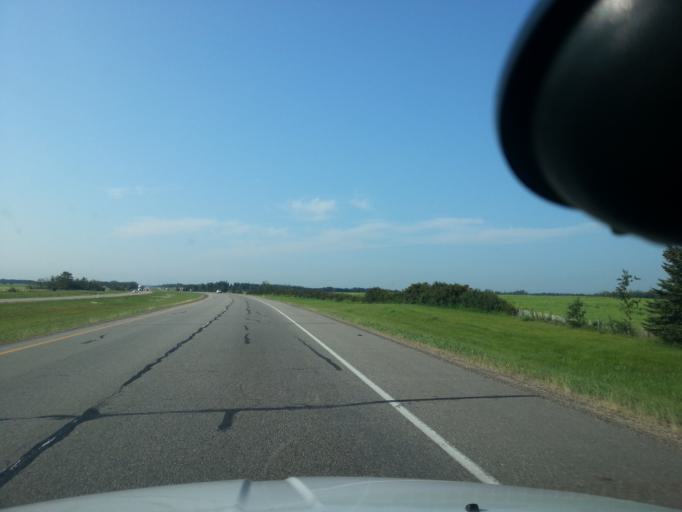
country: CA
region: Alberta
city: Millet
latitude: 52.9999
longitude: -113.6427
